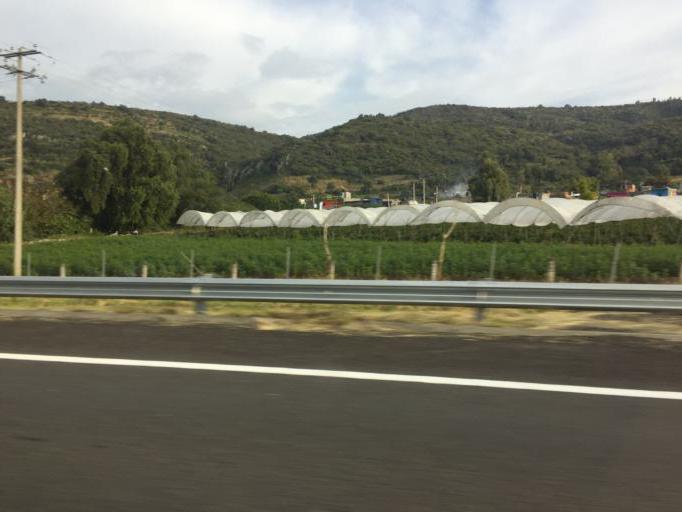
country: MX
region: Michoacan
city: Copandaro de Galeana
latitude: 19.8835
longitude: -101.1949
